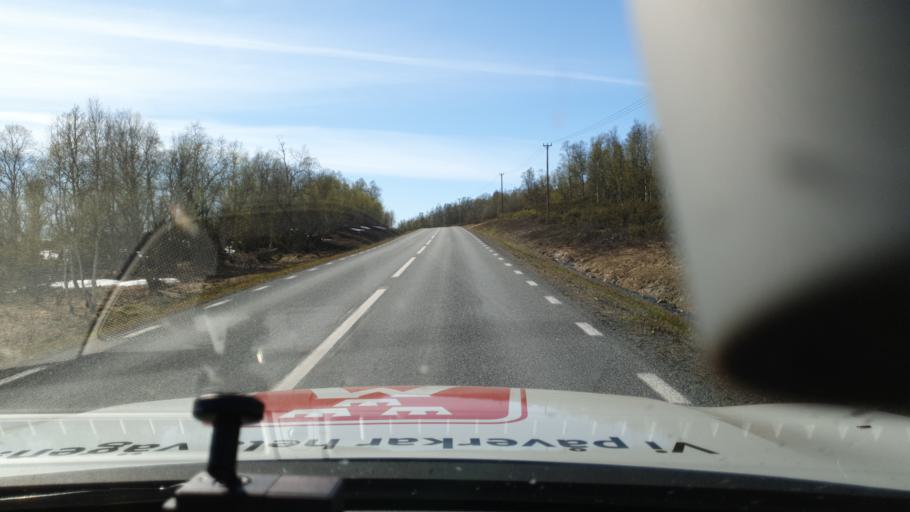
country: NO
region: Nordland
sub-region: Rana
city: Mo i Rana
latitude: 66.0381
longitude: 15.0390
